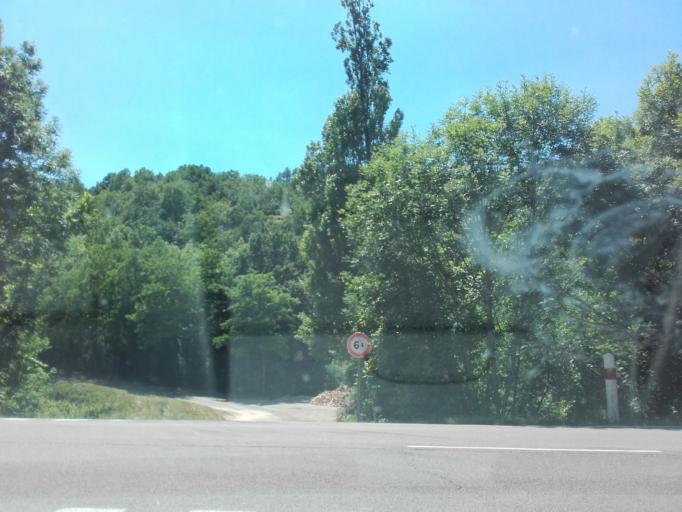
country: FR
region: Bourgogne
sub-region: Departement de la Cote-d'Or
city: Corpeau
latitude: 46.9505
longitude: 4.7255
